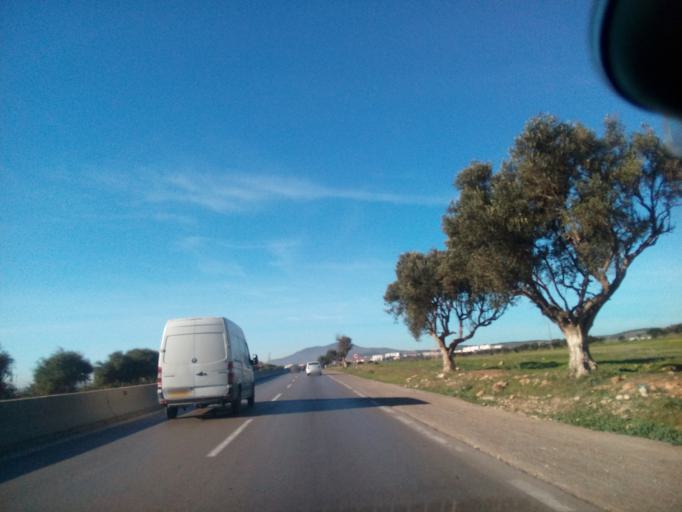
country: DZ
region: Oran
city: Ain el Bya
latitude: 35.7938
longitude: -0.3905
